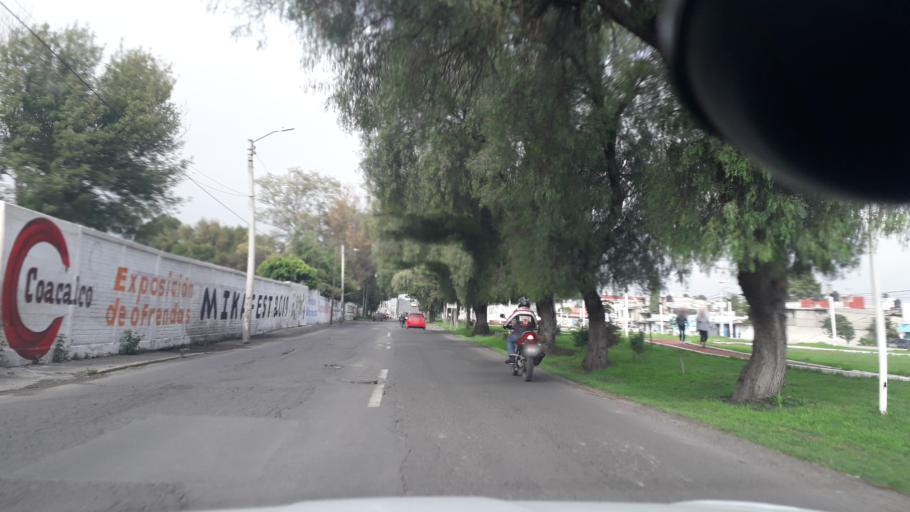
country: MX
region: Mexico
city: Coacalco
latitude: 19.6445
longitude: -99.0945
